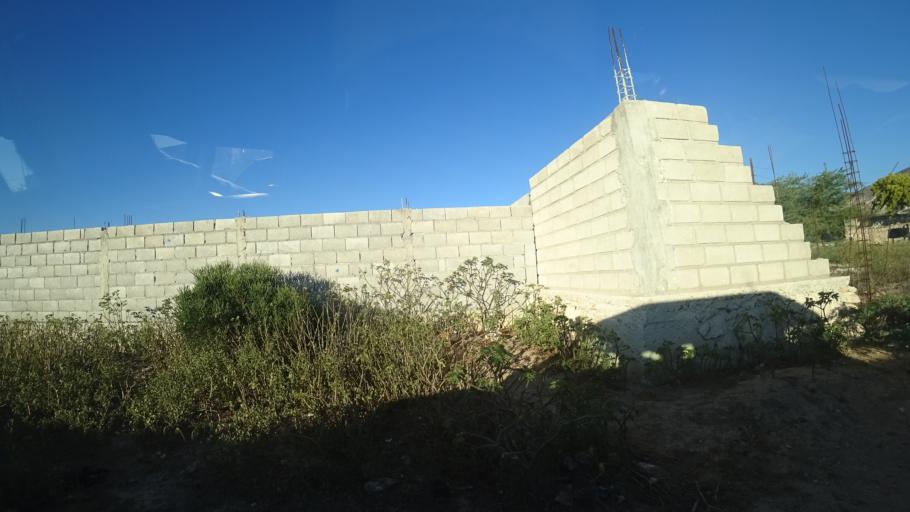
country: HT
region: Ouest
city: Croix des Bouquets
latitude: 18.6623
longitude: -72.2231
